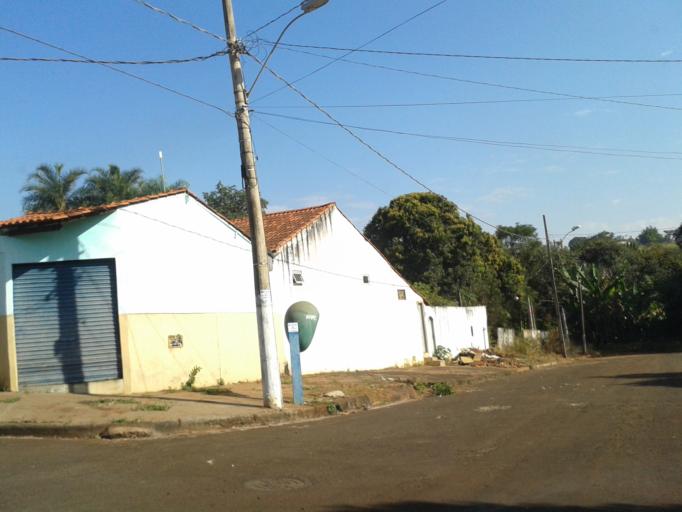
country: BR
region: Minas Gerais
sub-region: Ituiutaba
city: Ituiutaba
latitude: -18.9675
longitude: -49.4835
